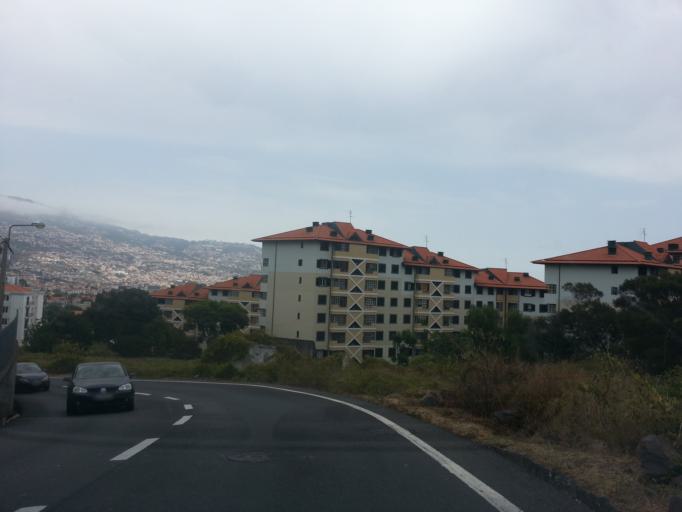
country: PT
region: Madeira
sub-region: Funchal
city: Funchal
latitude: 32.6469
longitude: -16.9319
